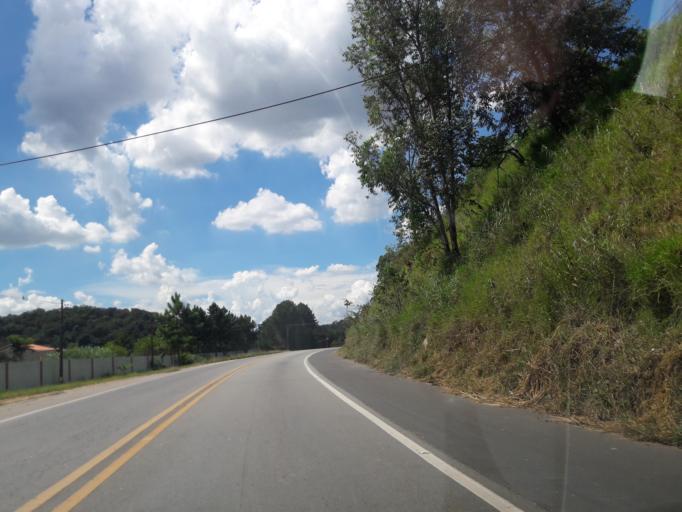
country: BR
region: Sao Paulo
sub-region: Campo Limpo Paulista
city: Campo Limpo Paulista
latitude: -23.2310
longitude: -46.7914
